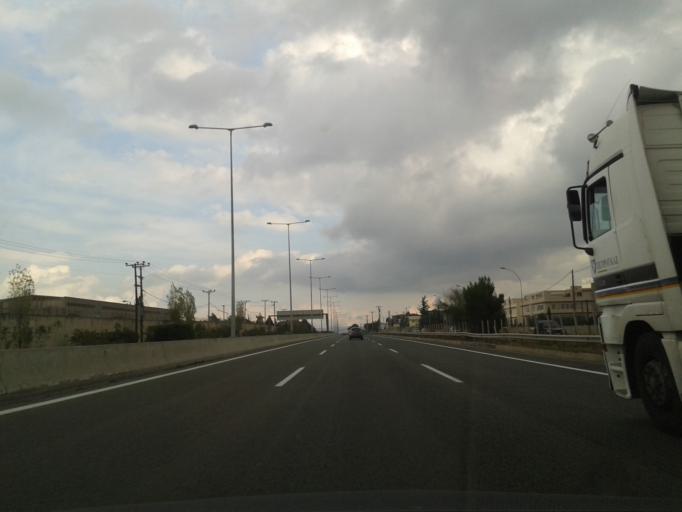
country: GR
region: Attica
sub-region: Nomarchia Anatolikis Attikis
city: Agios Stefanos
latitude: 38.1465
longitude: 23.8490
